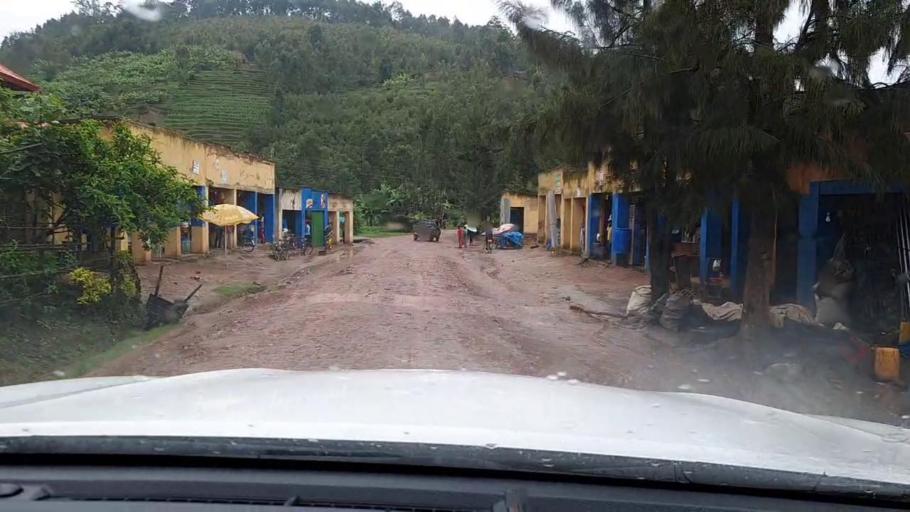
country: RW
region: Northern Province
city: Byumba
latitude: -1.7243
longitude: 29.9302
